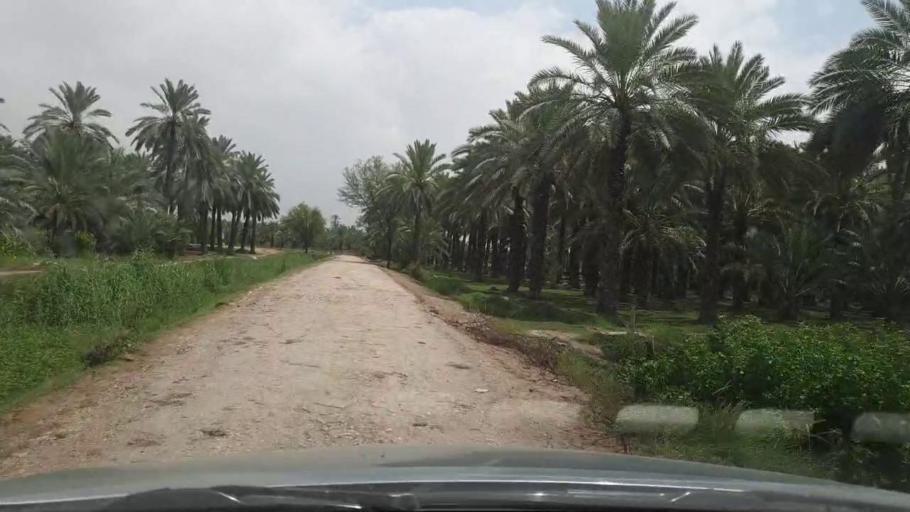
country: PK
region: Sindh
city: Kot Diji
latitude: 27.4103
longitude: 68.7618
